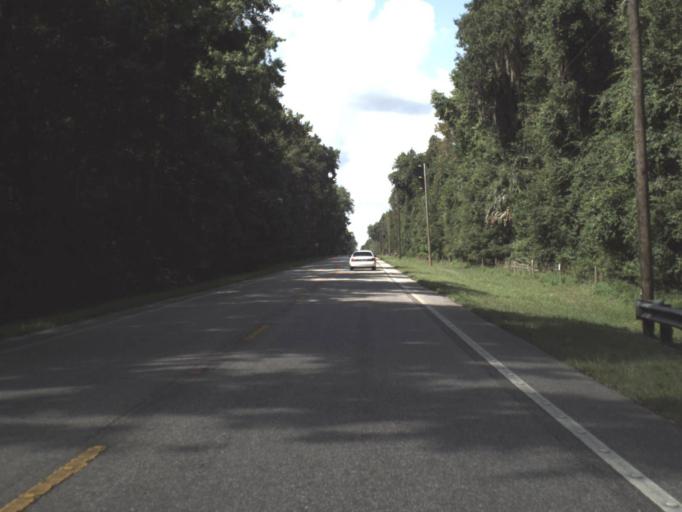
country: US
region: Florida
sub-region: Hernando County
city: North Brooksville
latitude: 28.6426
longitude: -82.3356
